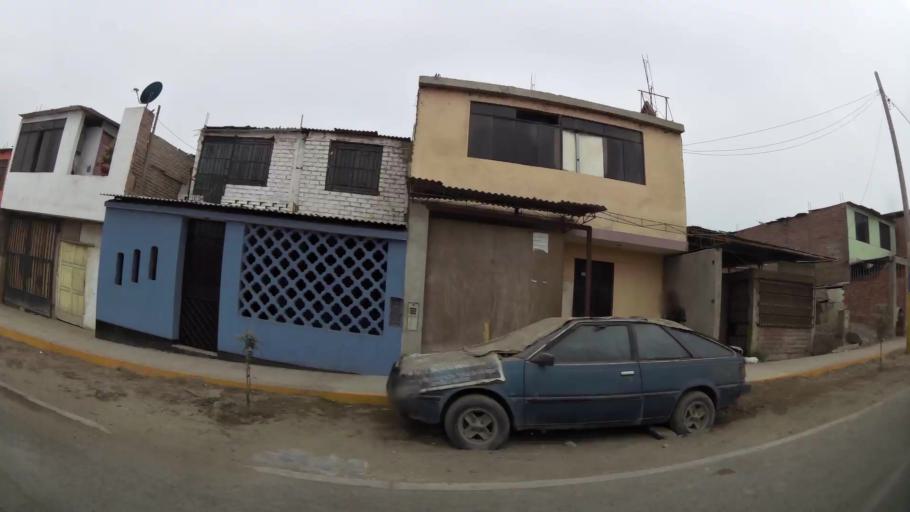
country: PE
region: Lima
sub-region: Lima
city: Surco
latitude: -12.2379
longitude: -76.9262
